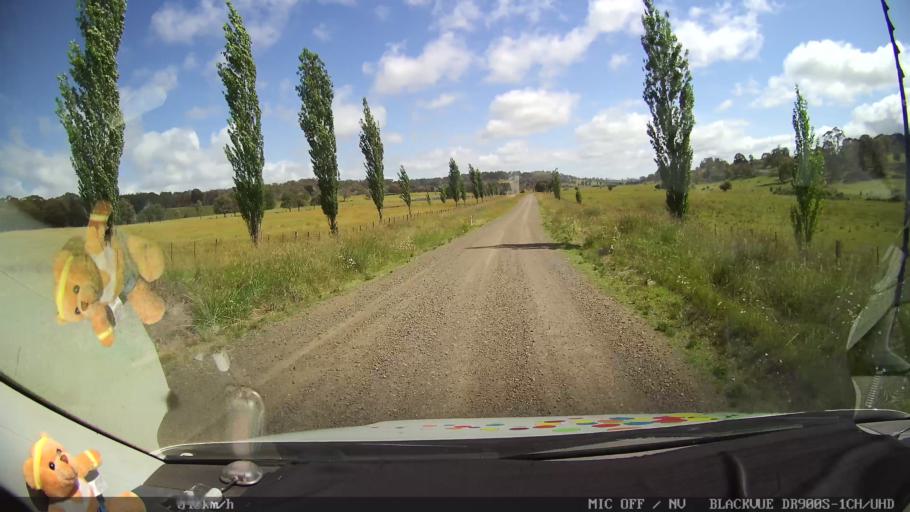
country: AU
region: New South Wales
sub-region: Glen Innes Severn
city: Glen Innes
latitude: -29.9731
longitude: 151.6992
